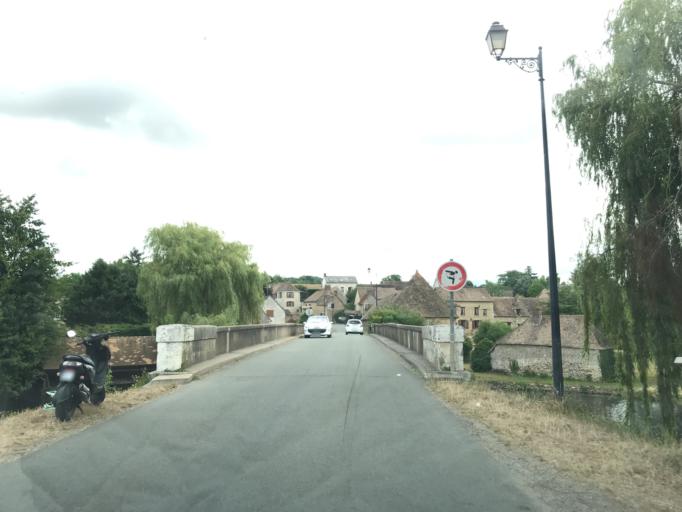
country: FR
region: Haute-Normandie
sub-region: Departement de l'Eure
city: Houlbec-Cocherel
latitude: 49.0745
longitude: 1.3040
